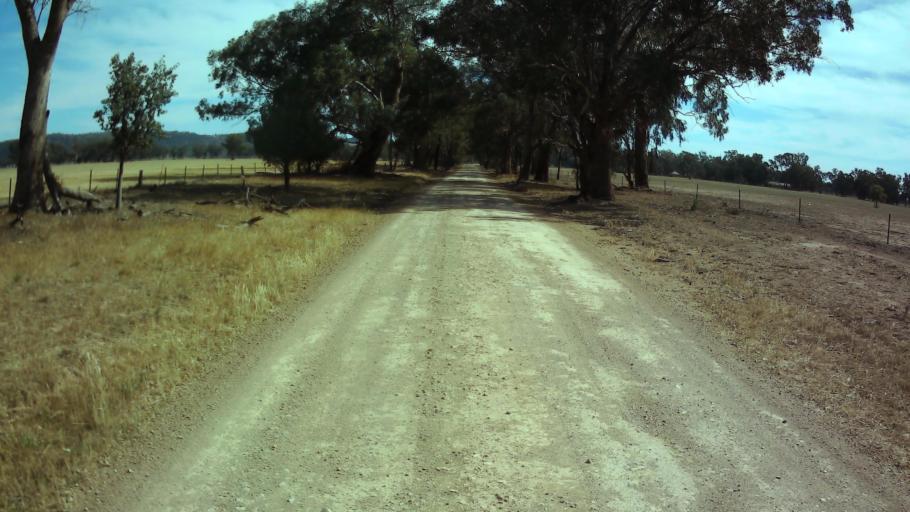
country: AU
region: New South Wales
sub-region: Weddin
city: Grenfell
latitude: -33.6991
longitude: 148.3024
